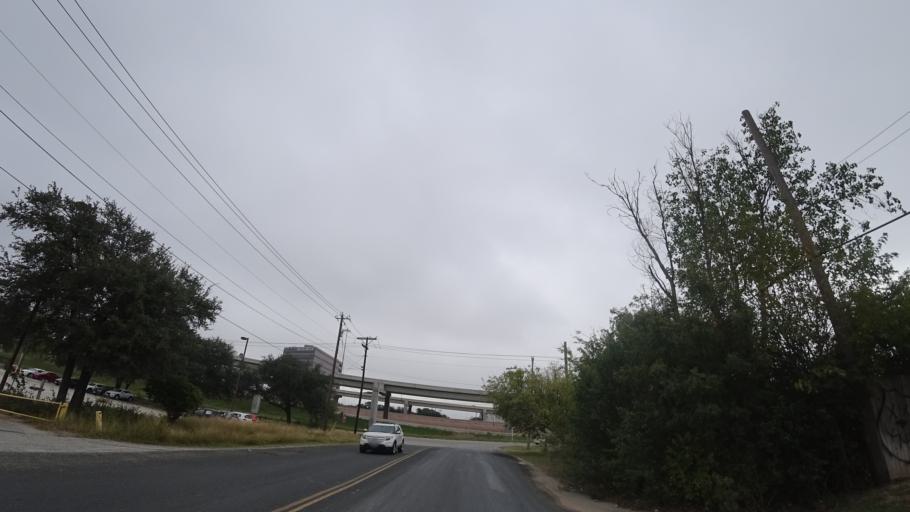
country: US
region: Texas
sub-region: Travis County
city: Austin
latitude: 30.2137
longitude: -97.7546
